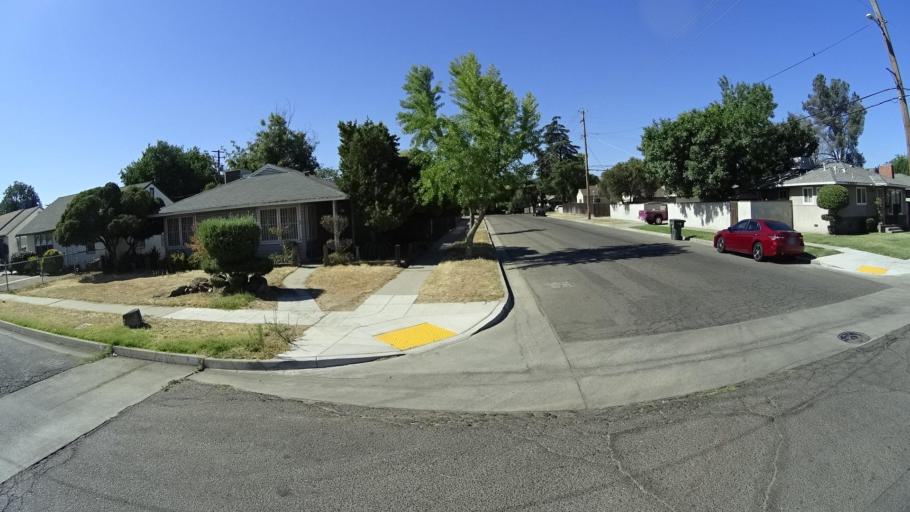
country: US
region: California
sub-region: Fresno County
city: Fresno
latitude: 36.7850
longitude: -119.7972
